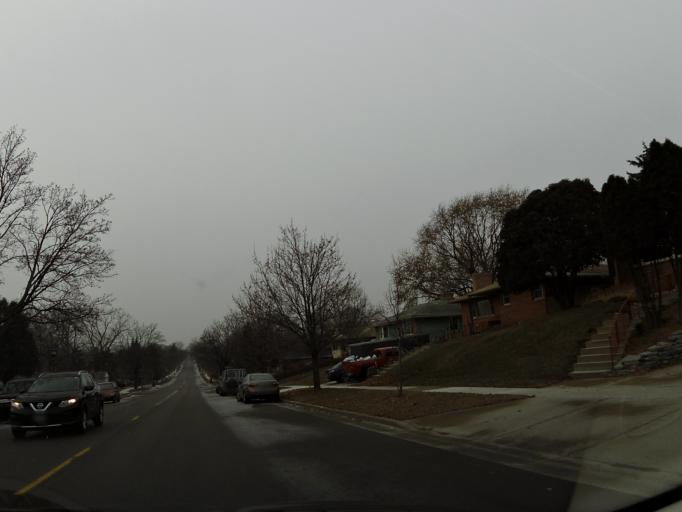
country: US
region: Minnesota
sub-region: Ramsey County
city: Maplewood
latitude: 44.9568
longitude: -93.0383
